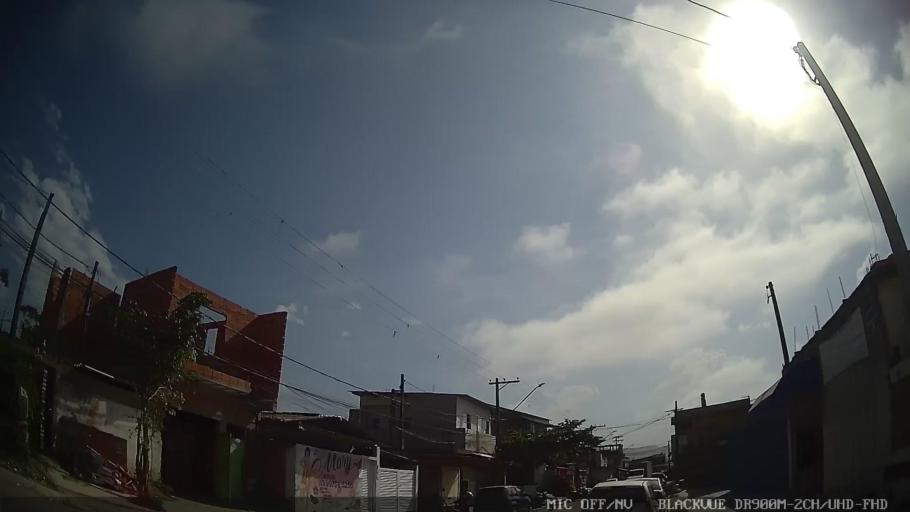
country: BR
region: Sao Paulo
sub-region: Guaruja
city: Guaruja
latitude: -23.9786
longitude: -46.1969
